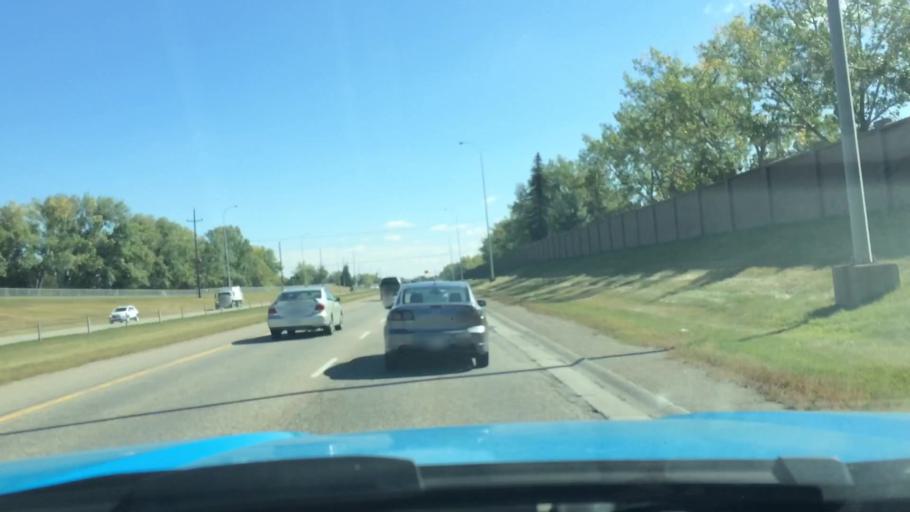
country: CA
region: Alberta
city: Calgary
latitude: 50.9481
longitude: -114.0514
